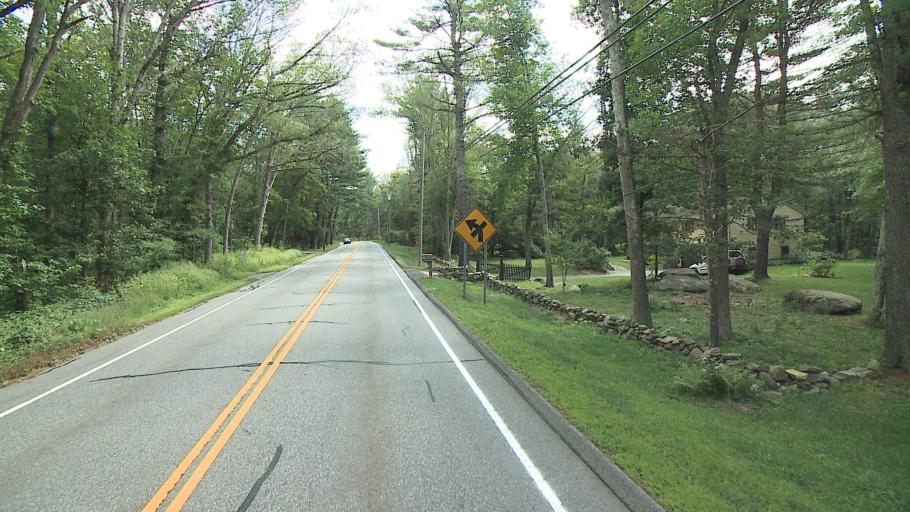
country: US
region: Connecticut
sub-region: Tolland County
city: Crystal Lake
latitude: 41.9192
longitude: -72.4162
